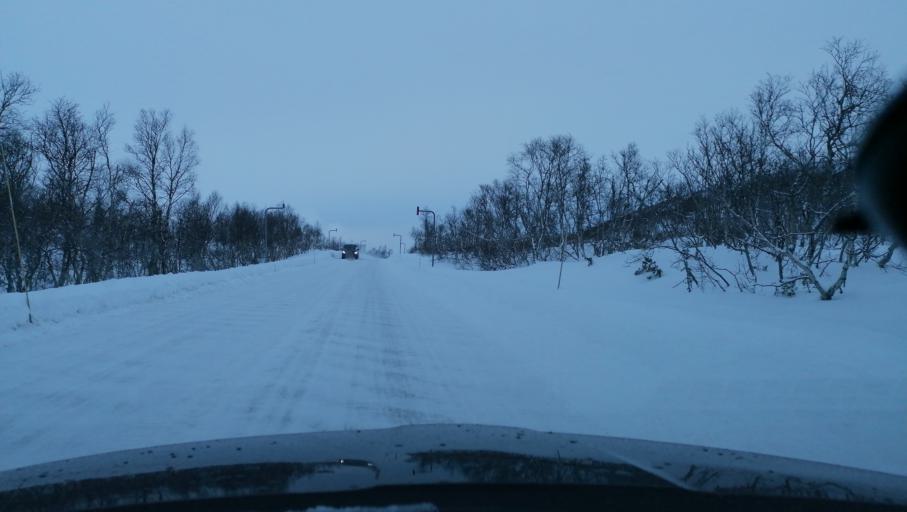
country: NO
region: Aust-Agder
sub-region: Bykle
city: Hovden
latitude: 59.6325
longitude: 7.4536
